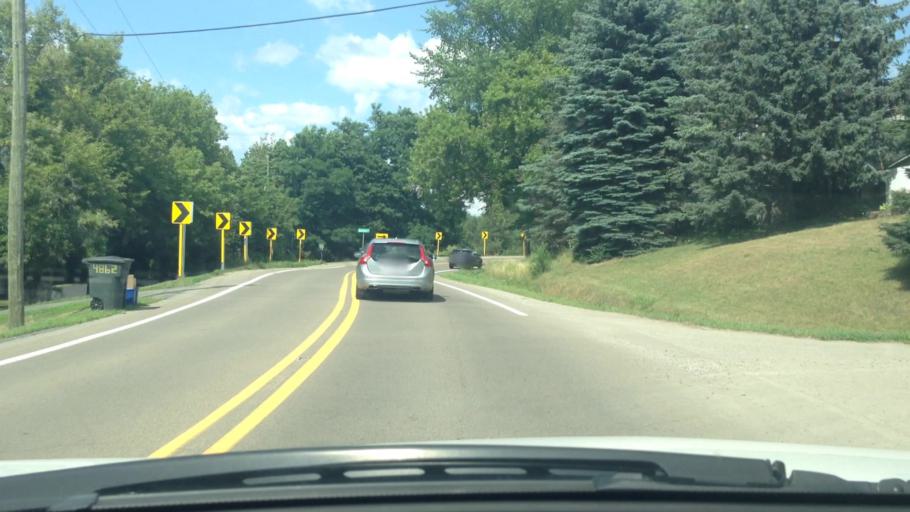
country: US
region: Michigan
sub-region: Oakland County
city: Clarkston
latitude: 42.7593
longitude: -83.3471
